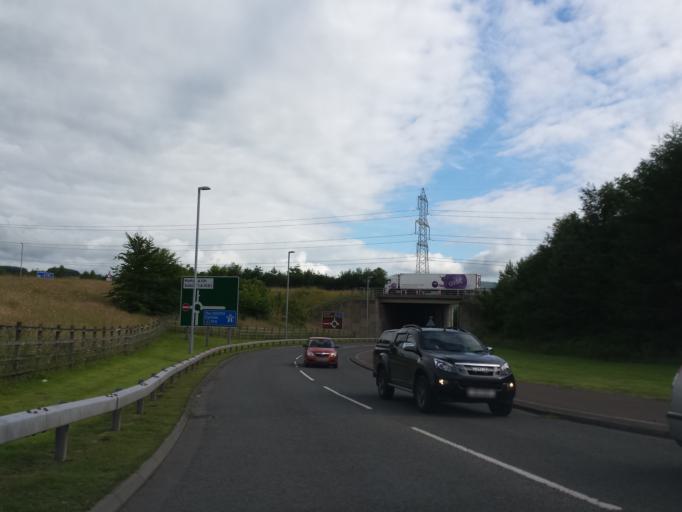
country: GB
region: Scotland
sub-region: Dumfries and Galloway
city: Moffat
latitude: 55.3123
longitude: -3.4543
